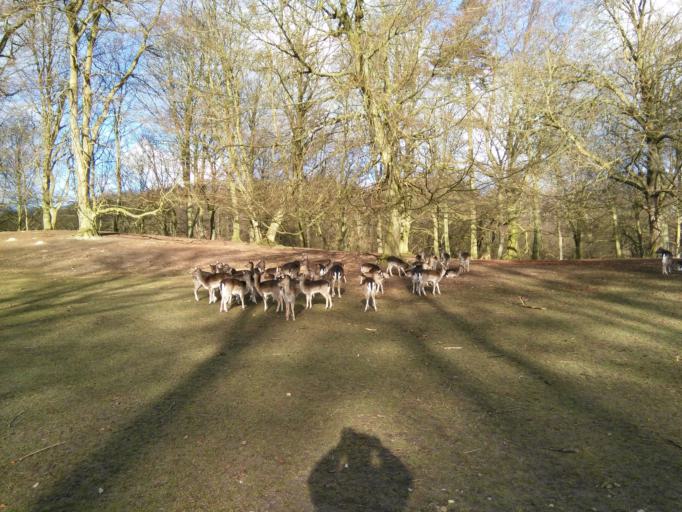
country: DK
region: Central Jutland
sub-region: Arhus Kommune
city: Arhus
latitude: 56.1224
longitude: 10.2178
